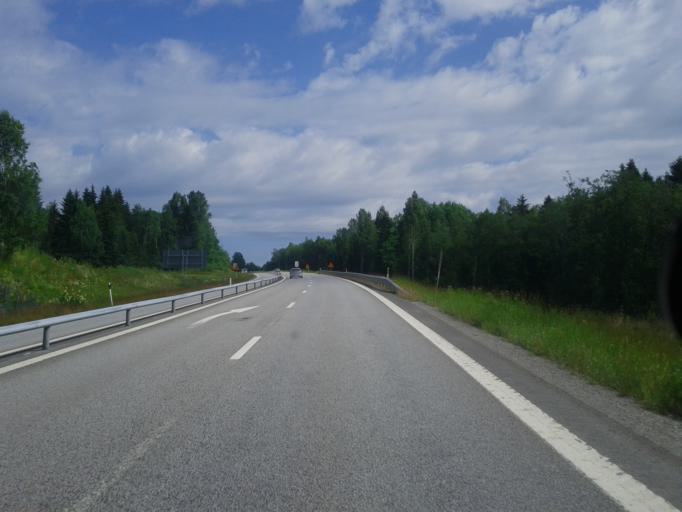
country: SE
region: Vaesternorrland
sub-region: OErnskoeldsviks Kommun
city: Ornskoldsvik
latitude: 63.2976
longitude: 18.8930
